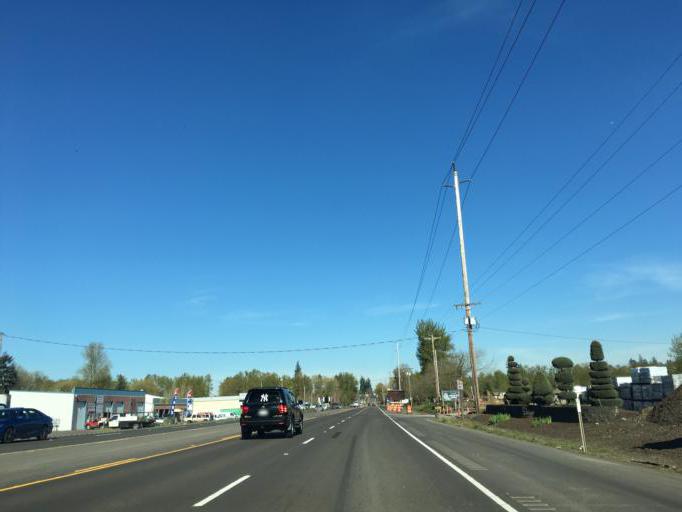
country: US
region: Oregon
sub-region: Clackamas County
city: Canby
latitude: 45.2534
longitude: -122.7157
